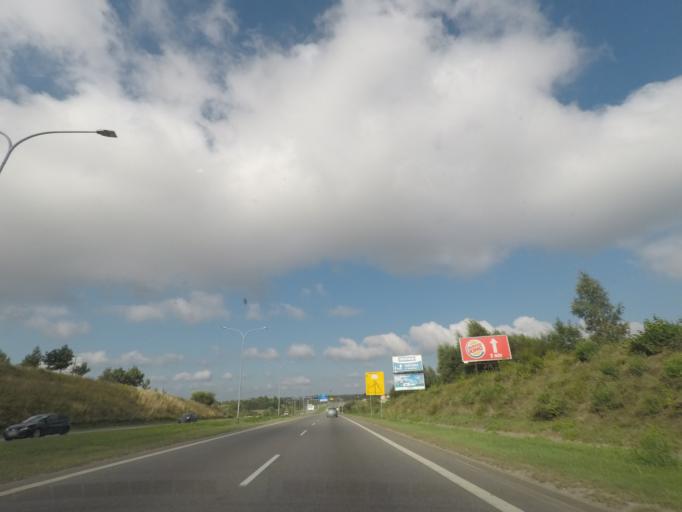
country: PL
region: Pomeranian Voivodeship
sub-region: Powiat gdanski
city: Kowale
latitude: 54.3357
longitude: 18.5816
